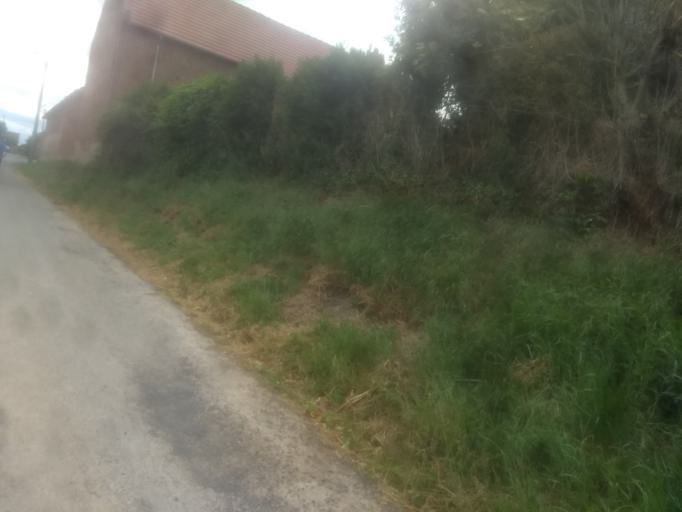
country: FR
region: Nord-Pas-de-Calais
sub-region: Departement du Pas-de-Calais
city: Beaurains
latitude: 50.2130
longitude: 2.8017
